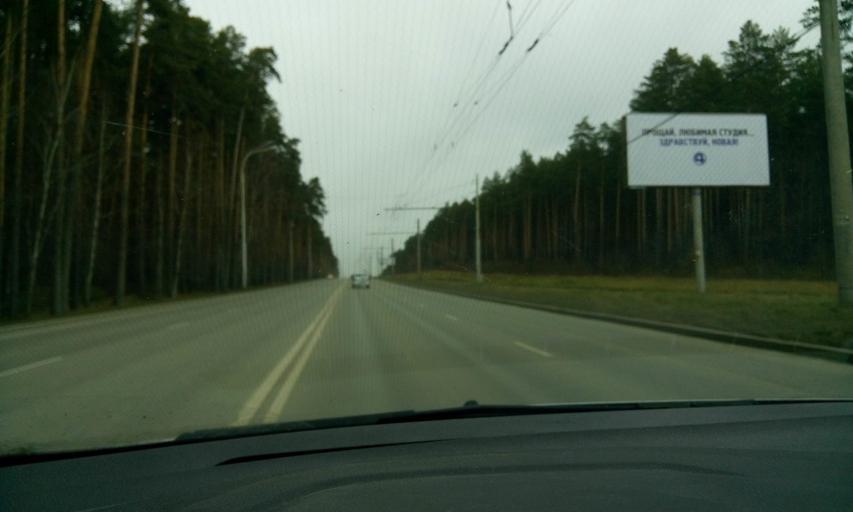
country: RU
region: Sverdlovsk
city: Sovkhoznyy
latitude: 56.7839
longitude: 60.5634
